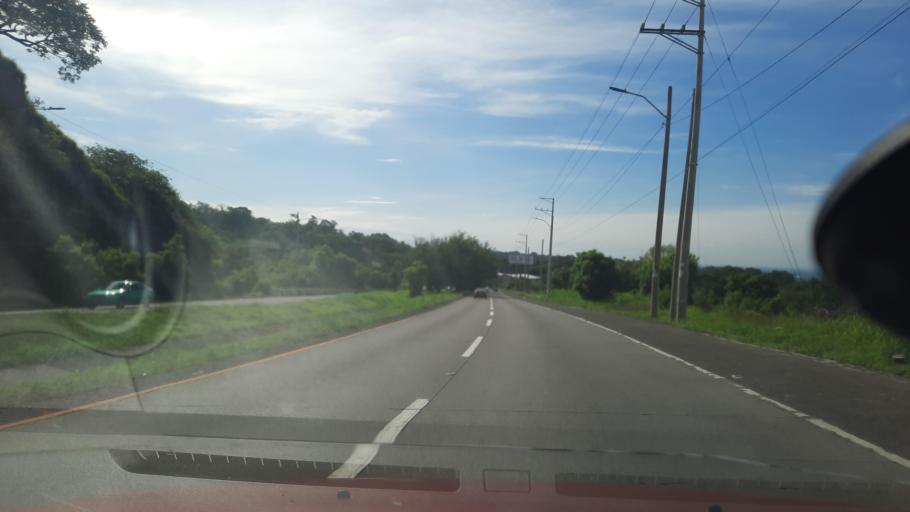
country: SV
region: La Paz
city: Olocuilta
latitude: 13.5252
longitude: -89.1099
